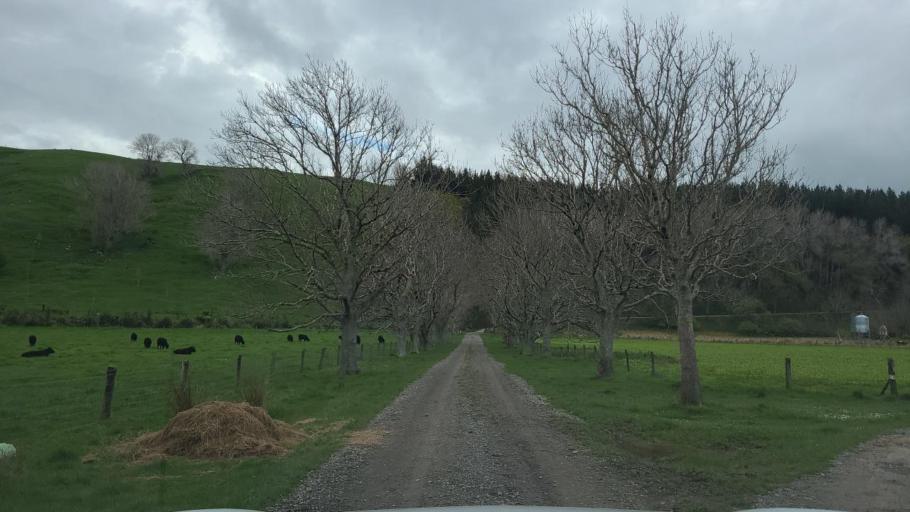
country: NZ
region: Wellington
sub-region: Masterton District
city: Masterton
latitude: -41.1698
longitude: 175.5896
